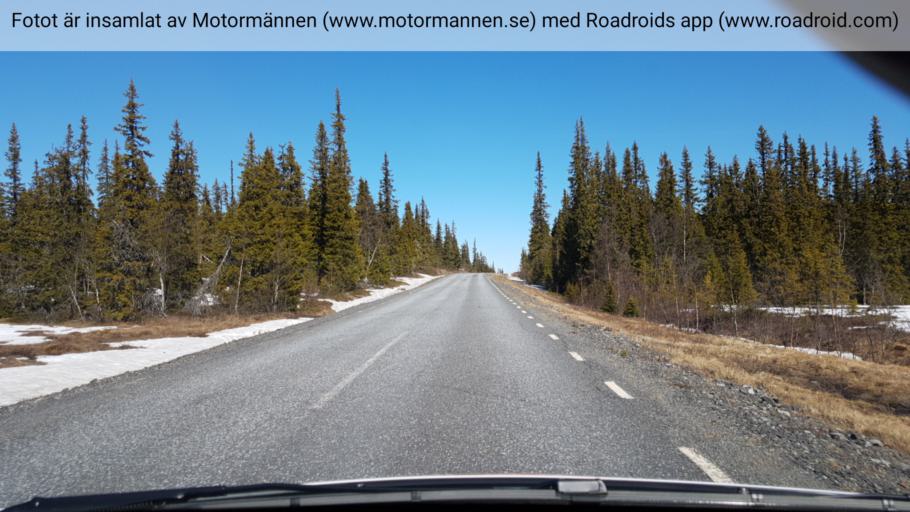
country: SE
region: Vaesterbotten
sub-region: Vilhelmina Kommun
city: Sjoberg
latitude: 65.0939
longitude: 15.8705
